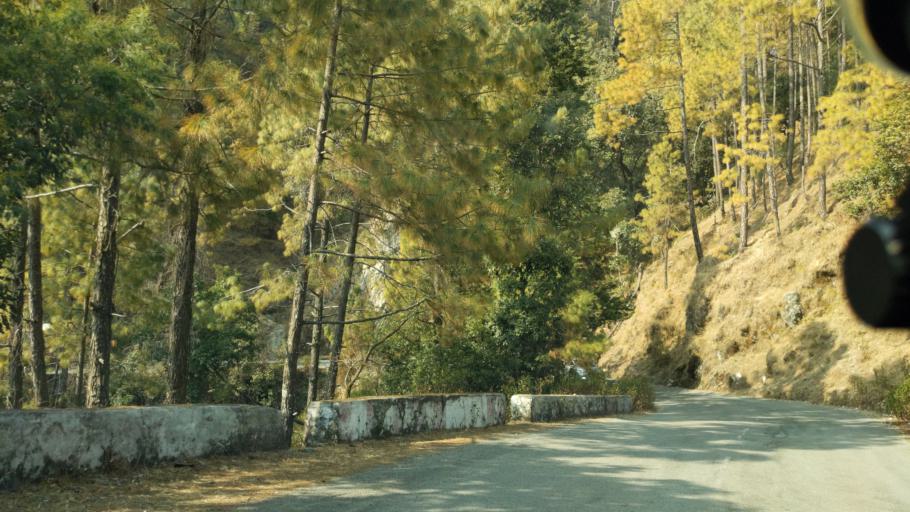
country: IN
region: Uttarakhand
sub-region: Naini Tal
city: Bhowali
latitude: 29.4025
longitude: 79.5385
